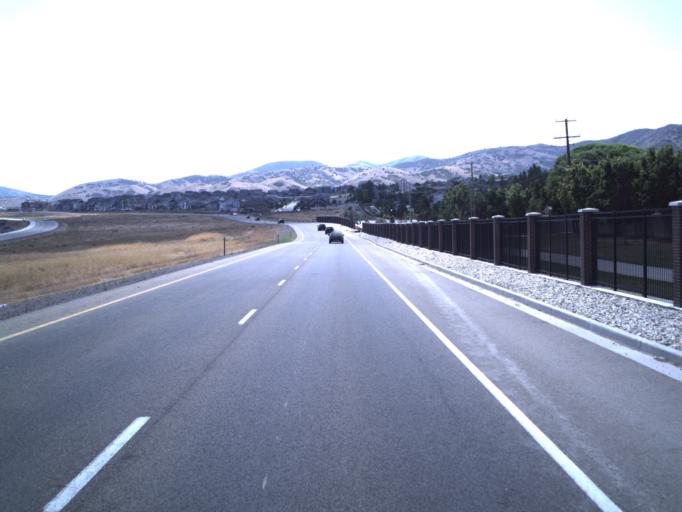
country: US
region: Utah
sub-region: Salt Lake County
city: Herriman
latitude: 40.4987
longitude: -112.0051
